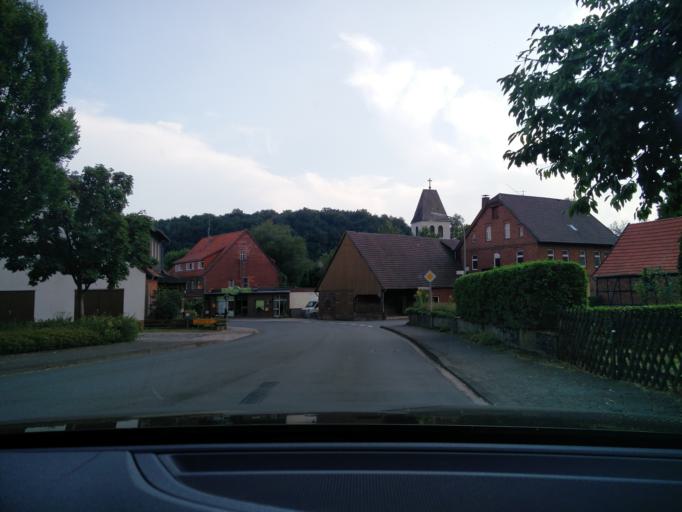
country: DE
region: North Rhine-Westphalia
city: Lichtenau
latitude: 51.6726
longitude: 8.9159
